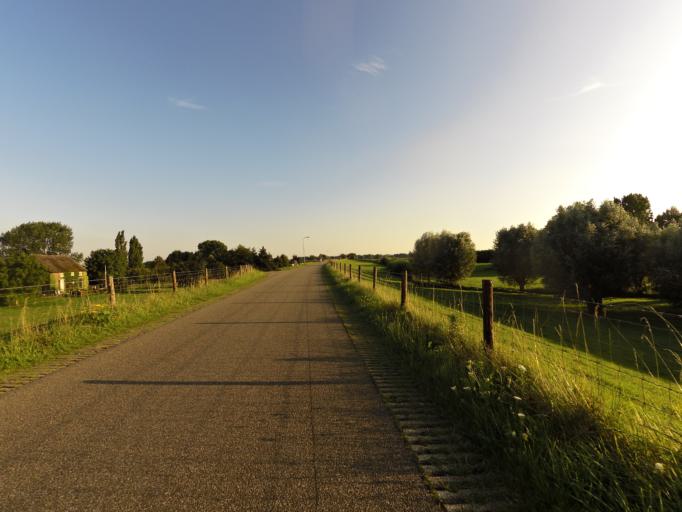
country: NL
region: Gelderland
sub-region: Gemeente Westervoort
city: Westervoort
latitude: 51.9386
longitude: 5.9693
